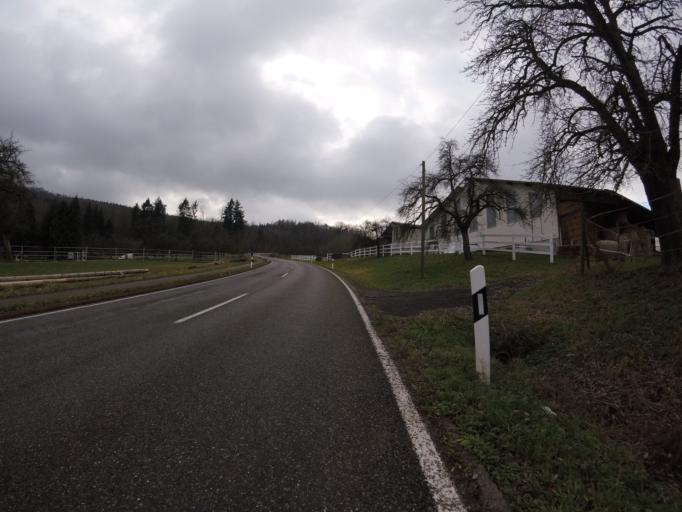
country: DE
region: Baden-Wuerttemberg
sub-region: Regierungsbezirk Stuttgart
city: Allmersbach im Tal
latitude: 48.9033
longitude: 9.4811
